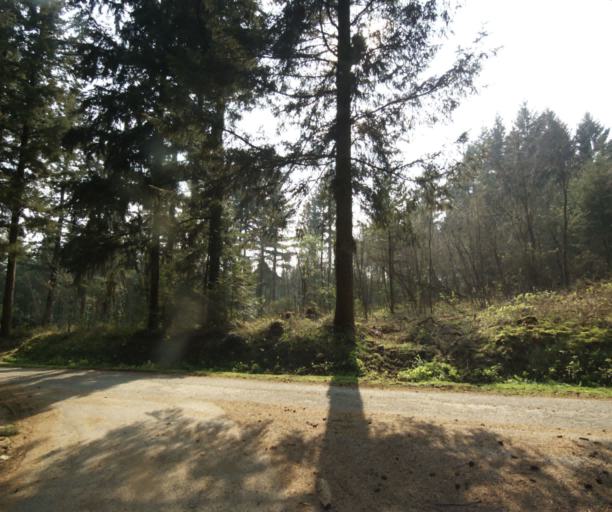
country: FR
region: Bourgogne
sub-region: Departement de Saone-et-Loire
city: Charolles
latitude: 46.4907
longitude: 4.4297
